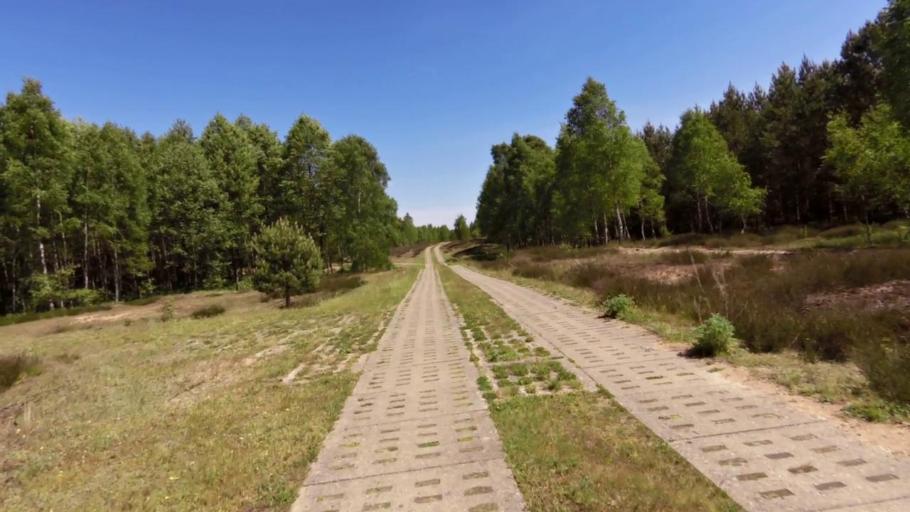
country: PL
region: West Pomeranian Voivodeship
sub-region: Powiat szczecinecki
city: Borne Sulinowo
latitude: 53.5725
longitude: 16.6338
